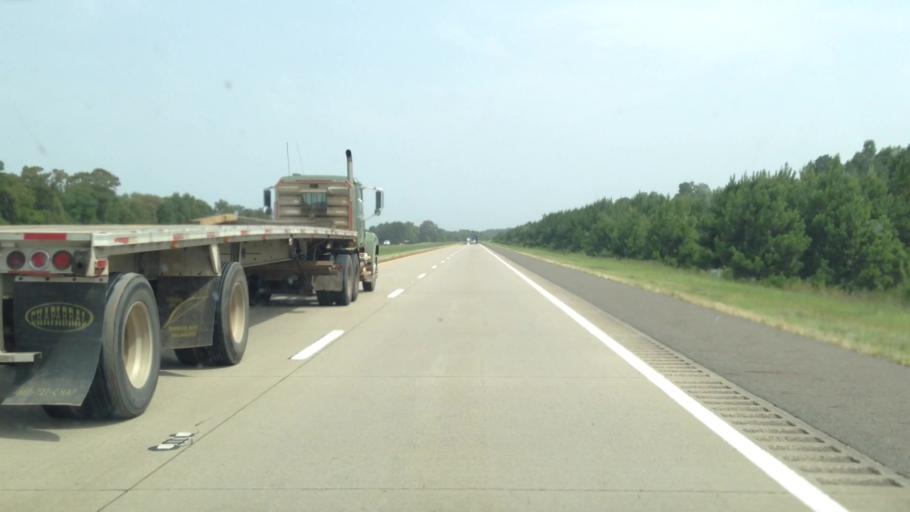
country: US
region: Texas
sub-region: Cass County
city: Queen City
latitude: 33.1908
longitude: -93.8775
